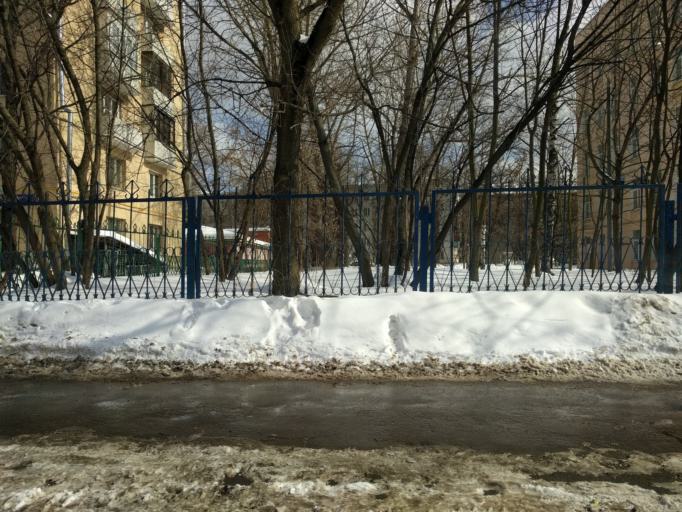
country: RU
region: Moscow
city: Metrogorodok
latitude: 55.7970
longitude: 37.7753
